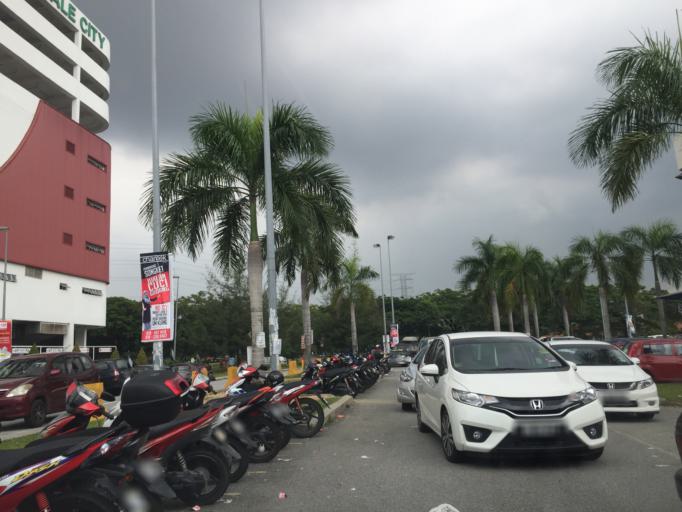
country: MY
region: Selangor
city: Klang
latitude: 2.9907
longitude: 101.4510
